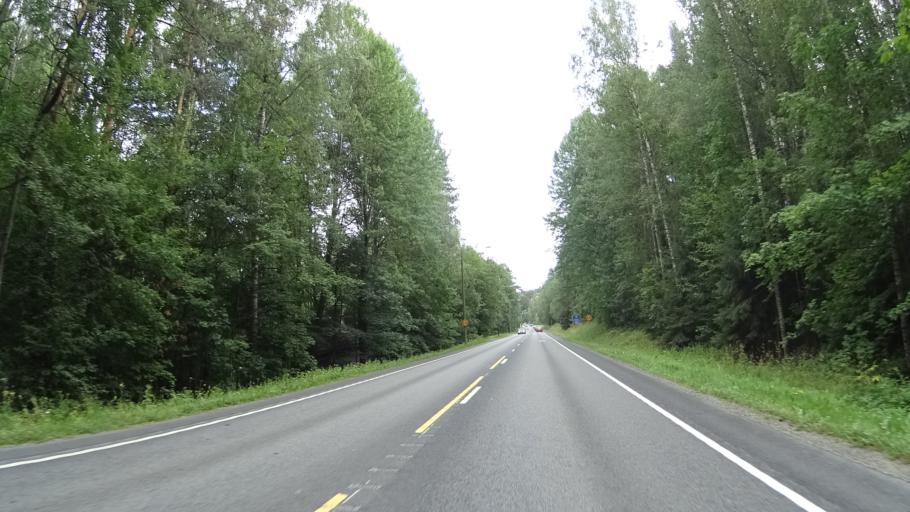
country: FI
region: Pirkanmaa
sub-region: Tampere
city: Kangasala
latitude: 61.4242
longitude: 24.1373
